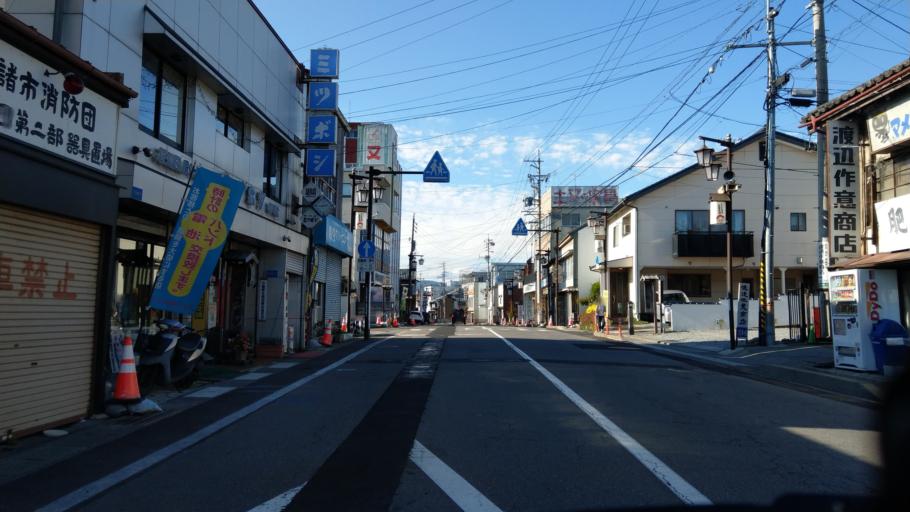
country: JP
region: Nagano
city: Komoro
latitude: 36.3239
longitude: 138.4308
